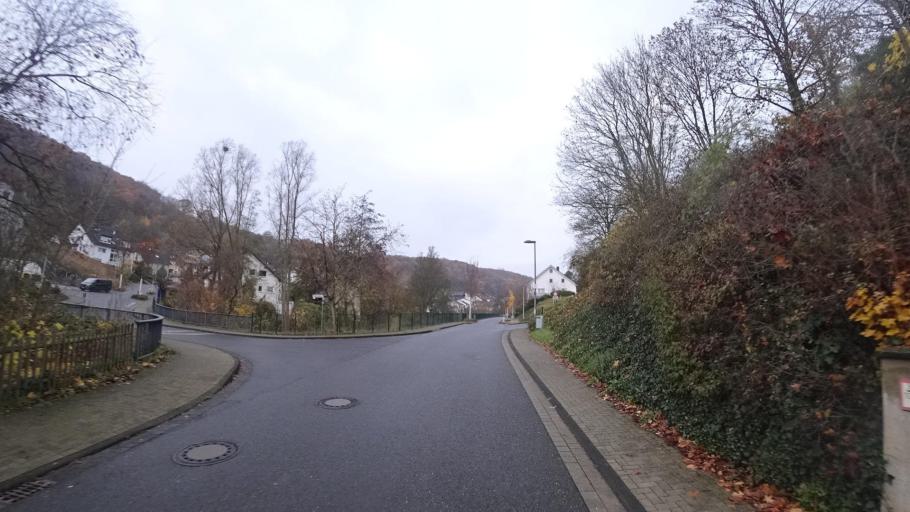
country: DE
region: Rheinland-Pfalz
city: Remagen
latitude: 50.5521
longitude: 7.1865
